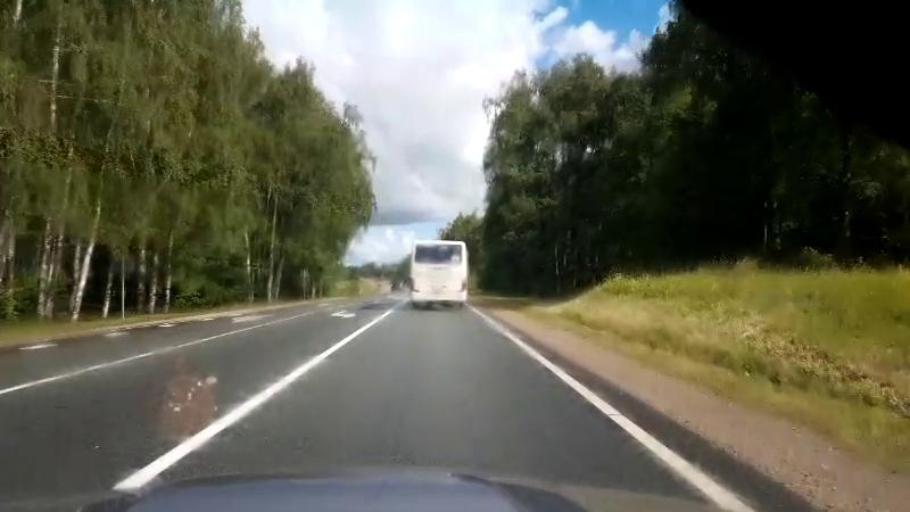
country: LV
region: Lecava
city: Iecava
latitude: 56.5173
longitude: 24.1731
